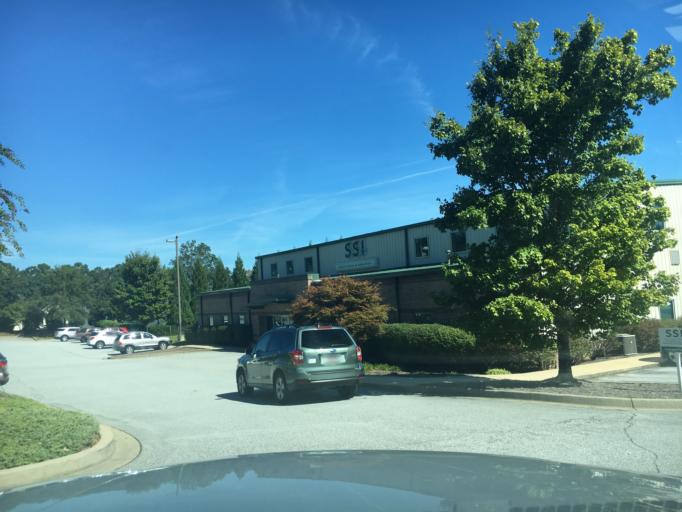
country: US
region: South Carolina
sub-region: Greenville County
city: Greer
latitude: 34.9502
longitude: -82.2335
